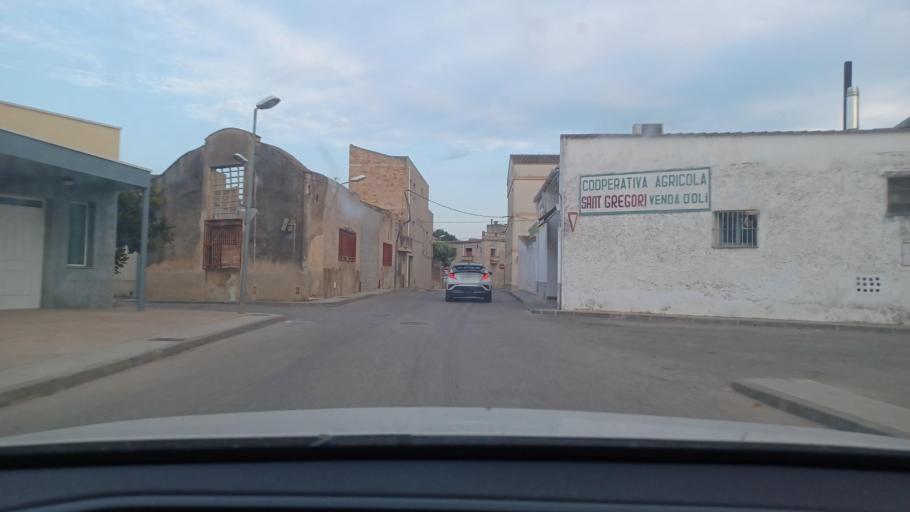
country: ES
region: Catalonia
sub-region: Provincia de Tarragona
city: Santa Barbara
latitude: 40.7144
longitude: 0.4894
